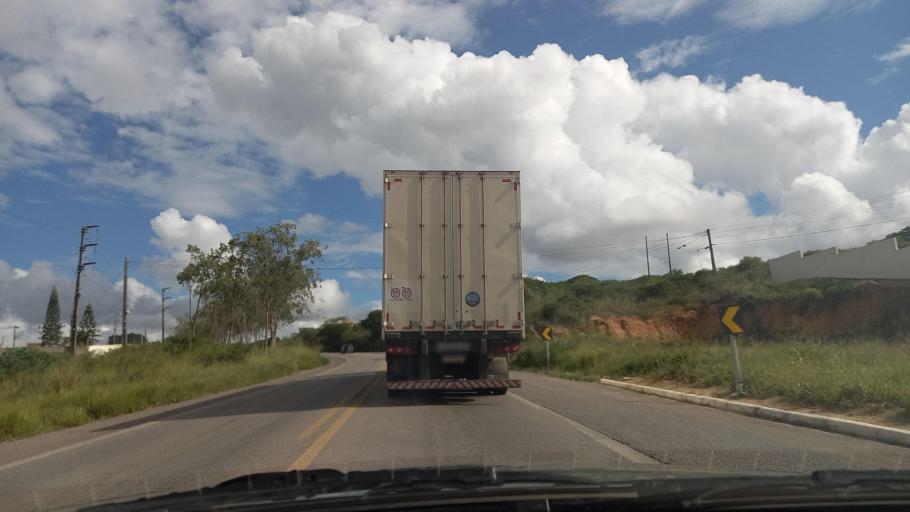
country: BR
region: Pernambuco
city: Garanhuns
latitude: -8.8577
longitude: -36.4643
